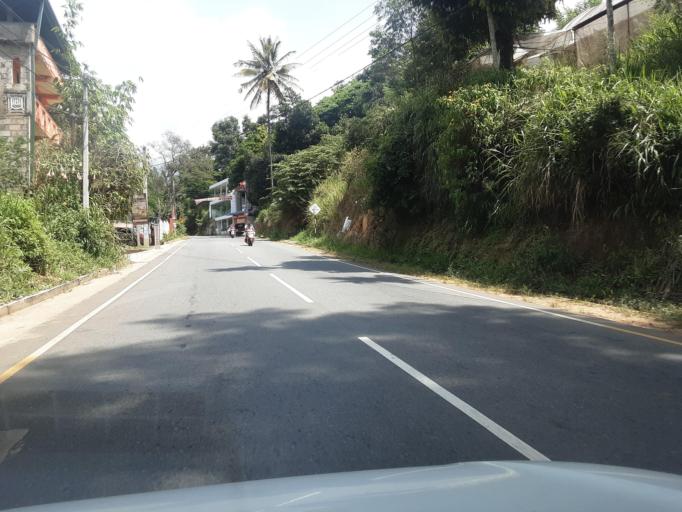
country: LK
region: Central
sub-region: Nuwara Eliya District
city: Nuwara Eliya
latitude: 6.9151
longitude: 80.9078
